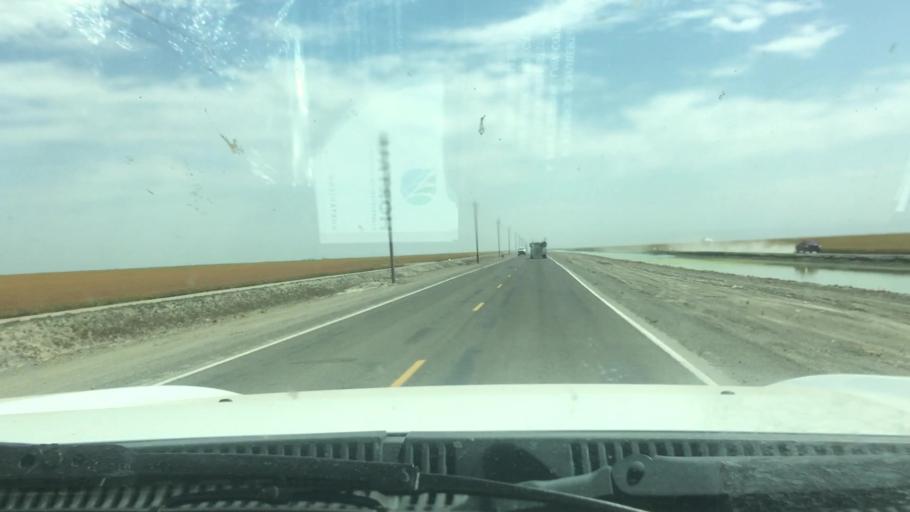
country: US
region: California
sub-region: Tulare County
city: Alpaugh
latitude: 35.9295
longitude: -119.5732
